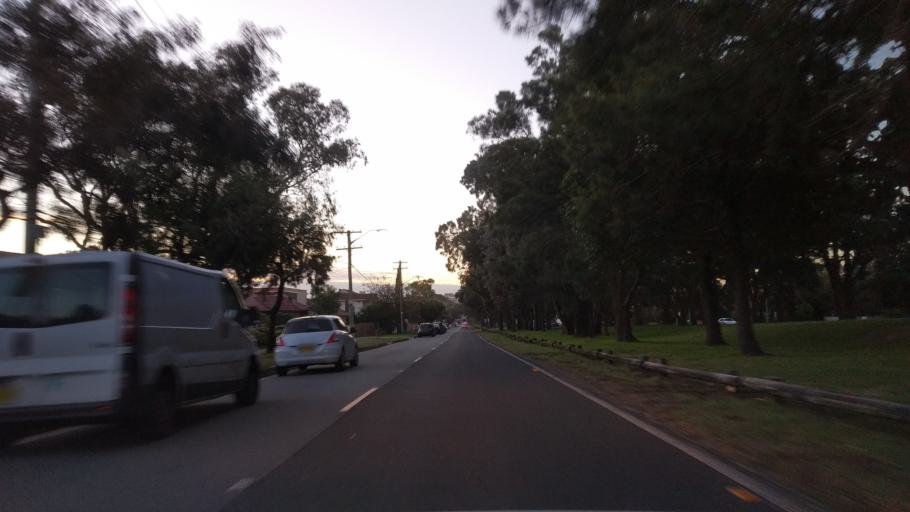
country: AU
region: New South Wales
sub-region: Randwick
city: Maroubra
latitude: -33.9523
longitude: 151.2416
